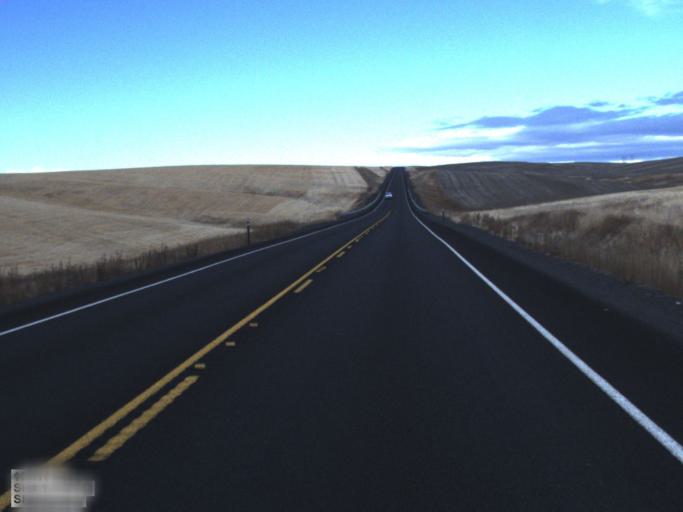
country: US
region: Washington
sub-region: Okanogan County
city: Coulee Dam
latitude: 47.8558
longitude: -118.8212
